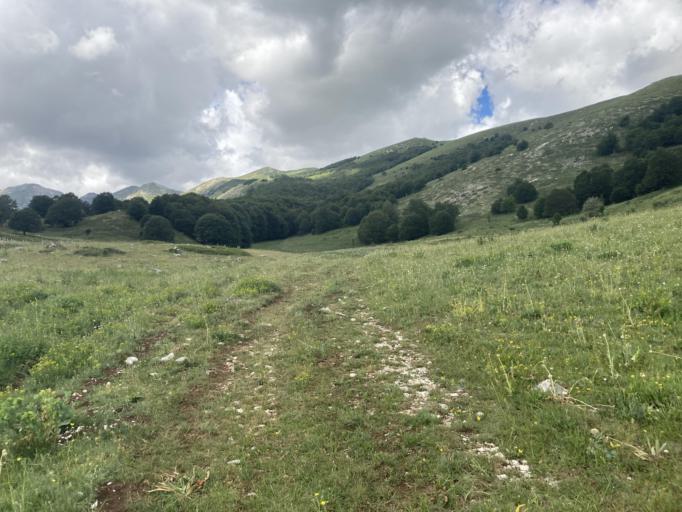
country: IT
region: Abruzzo
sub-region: Provincia dell' Aquila
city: Rocca di Cambio
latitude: 42.1903
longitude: 13.4578
